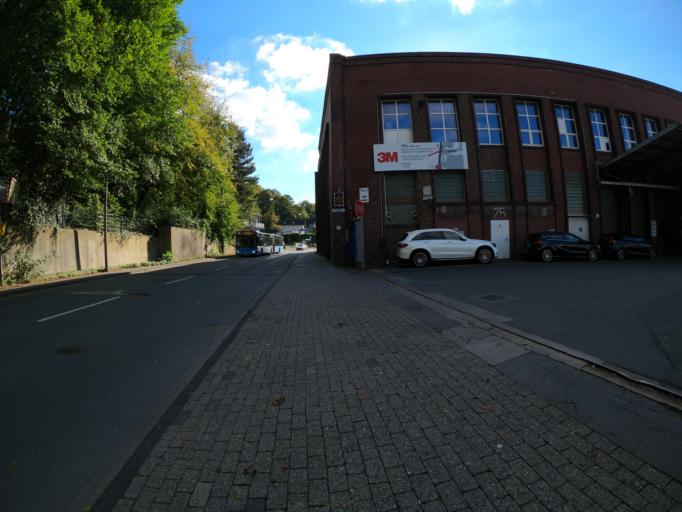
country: DE
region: North Rhine-Westphalia
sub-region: Regierungsbezirk Arnsberg
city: Schwelm
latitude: 51.2645
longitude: 7.2370
